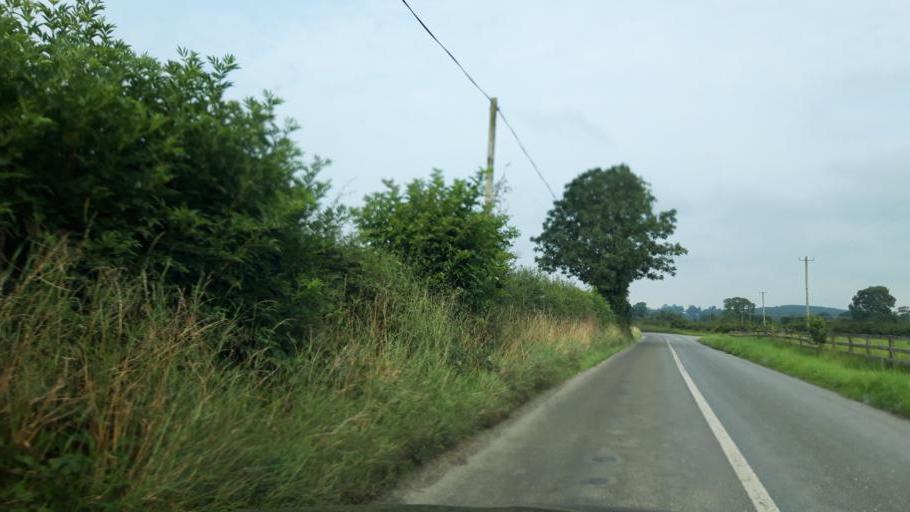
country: IE
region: Leinster
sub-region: Kilkenny
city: Callan
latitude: 52.5559
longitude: -7.5535
